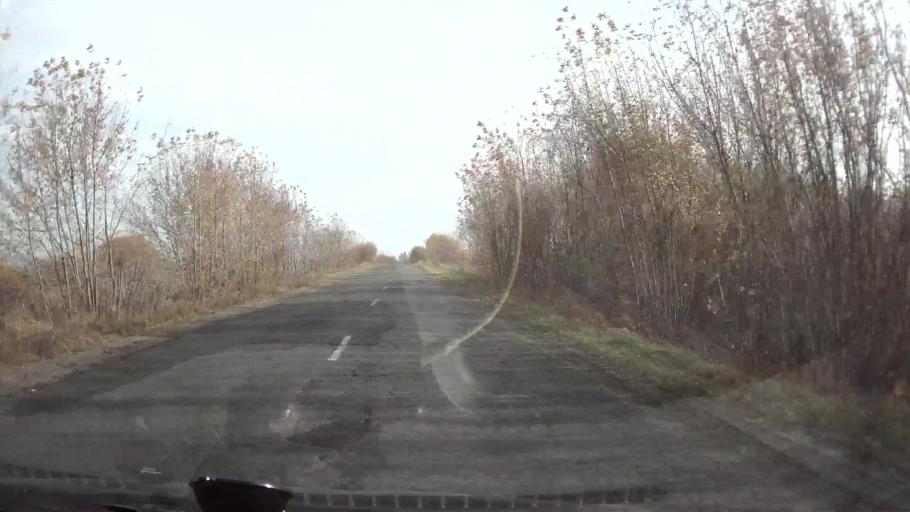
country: RU
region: Chuvashia
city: Alatyr'
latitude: 54.8446
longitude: 46.4647
